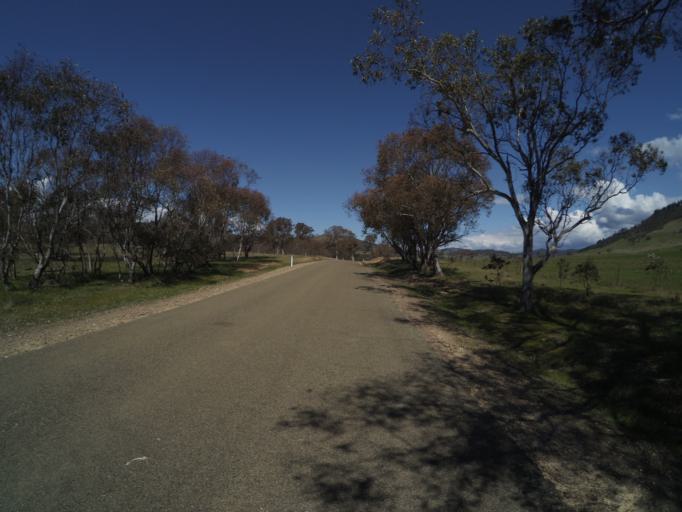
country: AU
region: Australian Capital Territory
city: Macquarie
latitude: -35.1400
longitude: 148.8767
